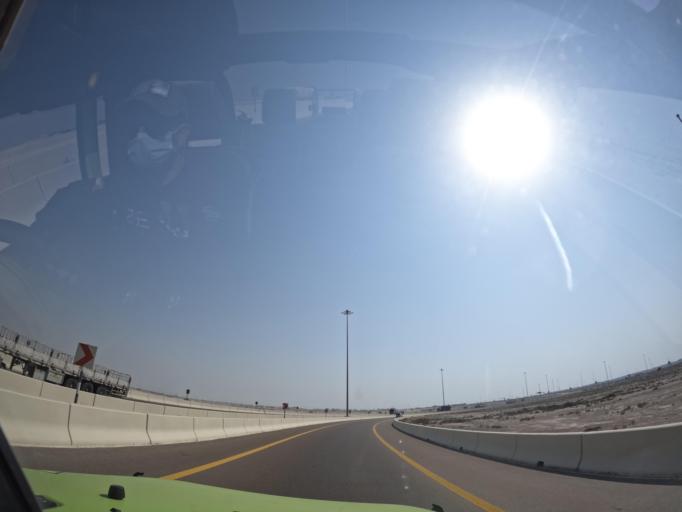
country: AE
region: Abu Dhabi
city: Abu Dhabi
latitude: 24.4069
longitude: 54.6768
